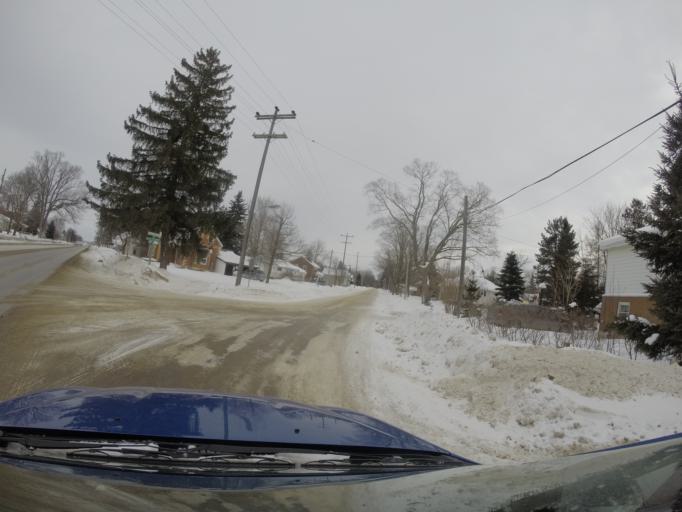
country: CA
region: Ontario
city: Wasaga Beach
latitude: 44.4208
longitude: -80.0845
